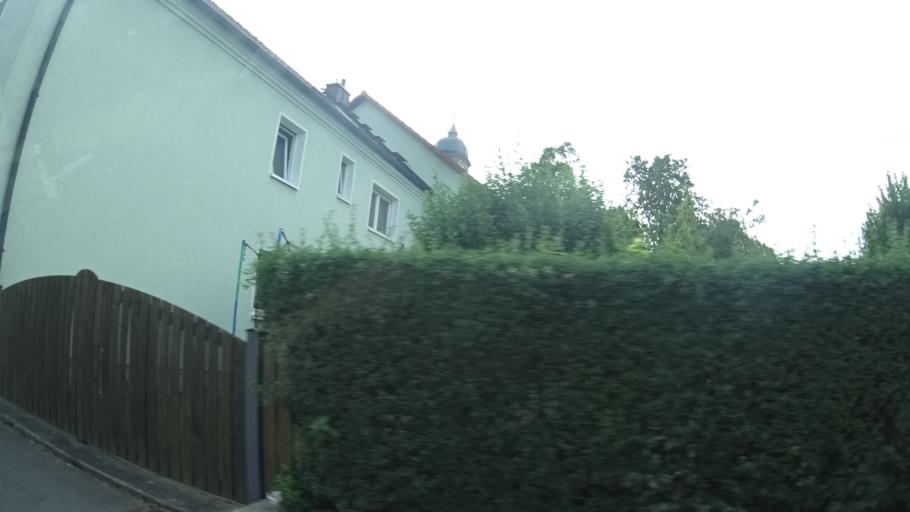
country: DE
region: Bavaria
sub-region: Regierungsbezirk Unterfranken
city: Helmstadt
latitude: 49.7626
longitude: 9.7112
